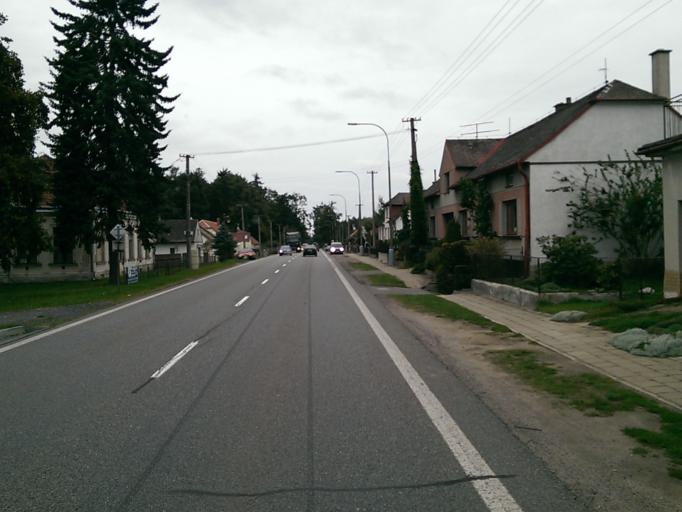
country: CZ
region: Vysocina
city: Zeletava
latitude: 49.1271
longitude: 15.6956
